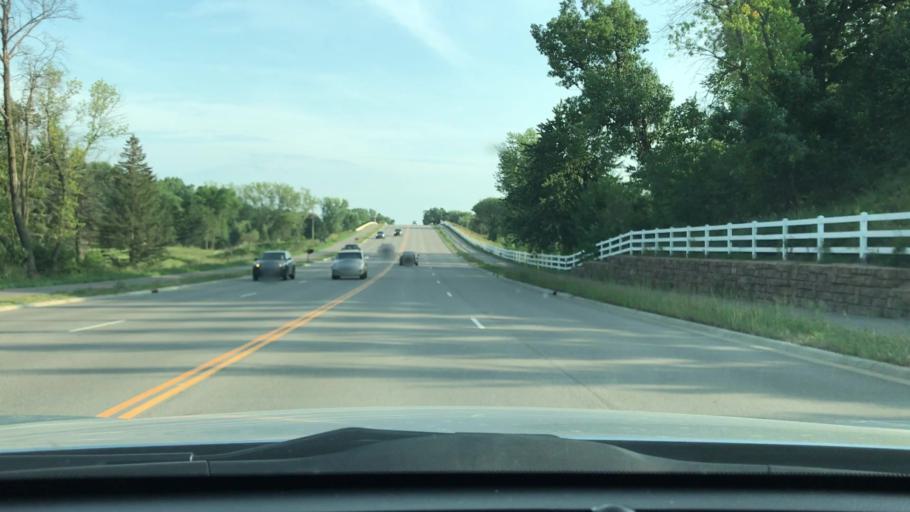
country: US
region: Minnesota
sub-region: Hennepin County
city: Maple Grove
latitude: 45.0535
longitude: -93.4819
